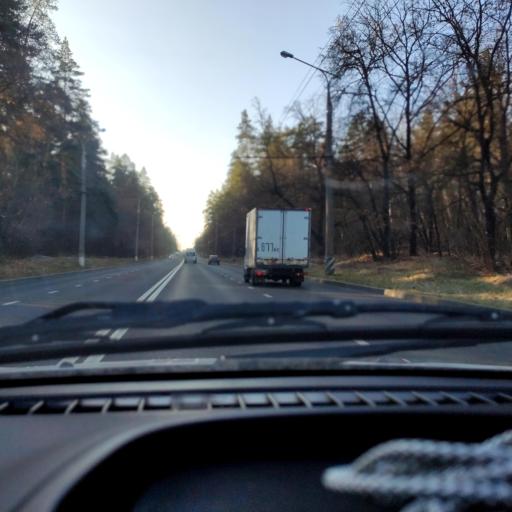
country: RU
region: Samara
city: Zhigulevsk
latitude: 53.4987
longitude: 49.4632
